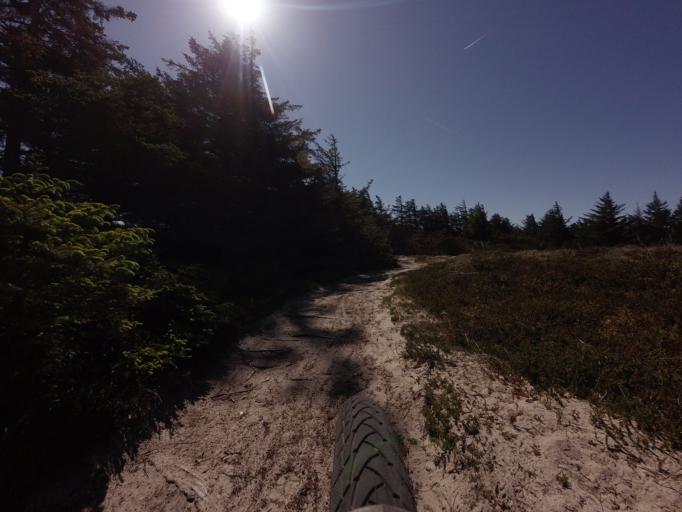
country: DK
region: North Denmark
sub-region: Jammerbugt Kommune
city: Pandrup
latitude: 57.2936
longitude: 9.6459
